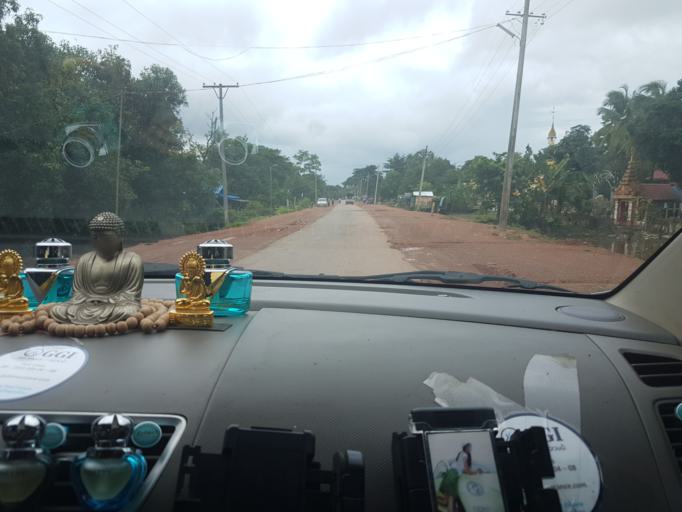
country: MM
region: Bago
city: Nyaunglebin
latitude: 17.9150
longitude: 96.8369
